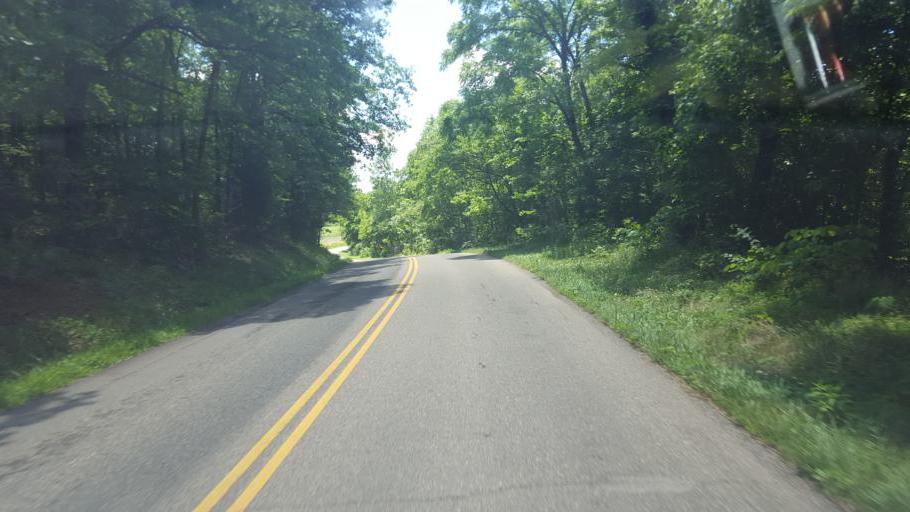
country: US
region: Ohio
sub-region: Gallia County
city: Gallipolis
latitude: 38.7780
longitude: -82.3871
